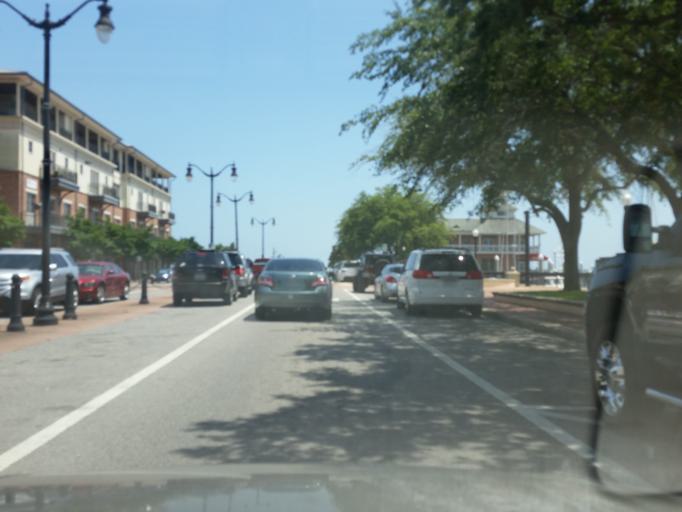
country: US
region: Florida
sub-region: Escambia County
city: Pensacola
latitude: 30.4039
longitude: -87.2134
